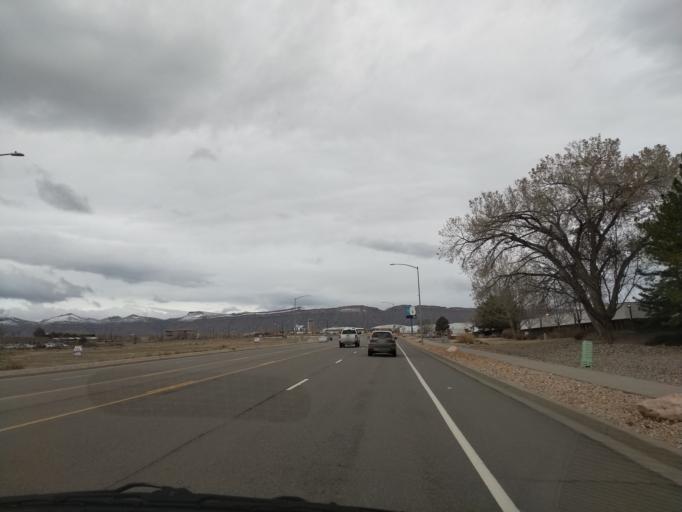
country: US
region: Colorado
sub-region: Mesa County
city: Fruitvale
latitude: 39.1159
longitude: -108.5320
